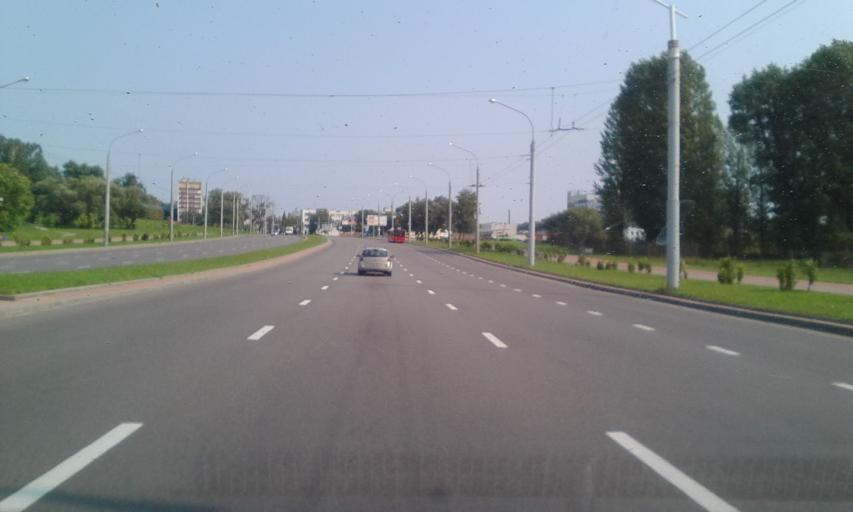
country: BY
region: Minsk
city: Novoye Medvezhino
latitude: 53.8705
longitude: 27.4956
